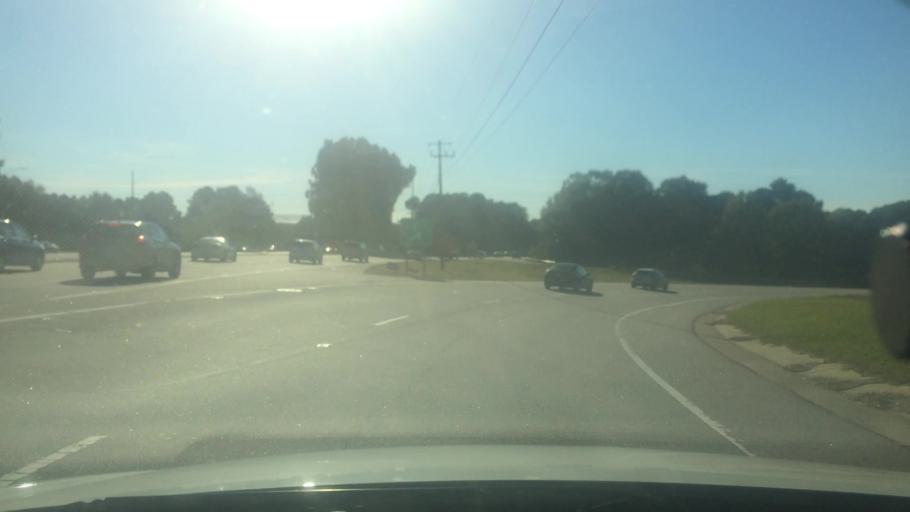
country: US
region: North Carolina
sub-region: Wake County
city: Raleigh
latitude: 35.8158
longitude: -78.6028
